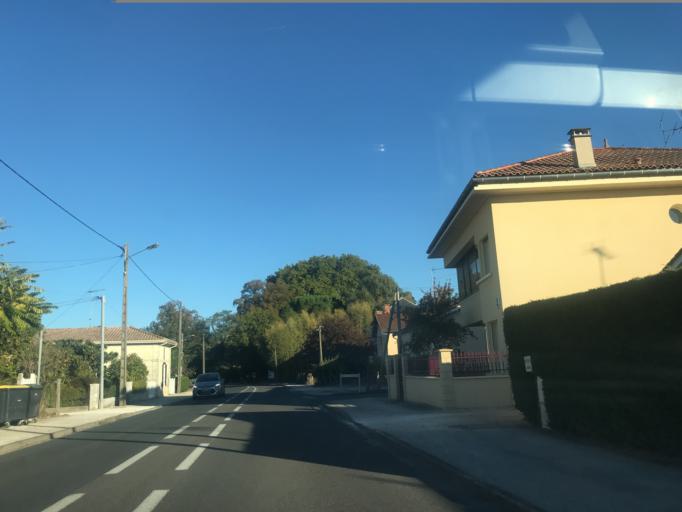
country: FR
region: Poitou-Charentes
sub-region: Departement de la Charente-Maritime
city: Saint-Aigulin
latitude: 45.1568
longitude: -0.0022
